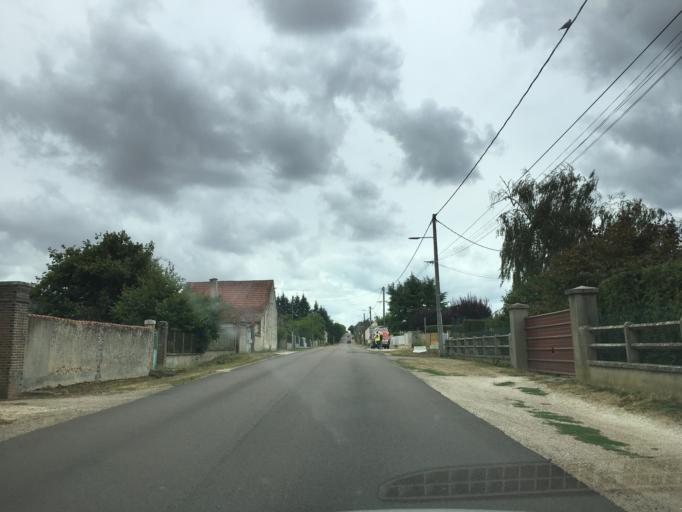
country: FR
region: Bourgogne
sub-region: Departement de l'Yonne
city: Joigny
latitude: 47.9565
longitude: 3.3770
